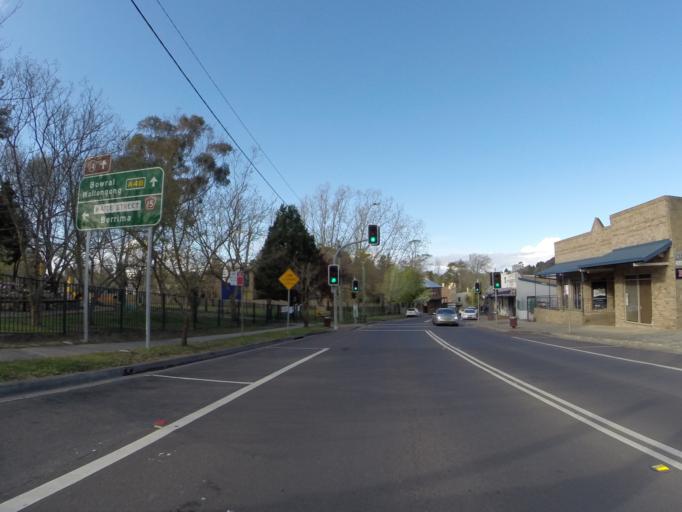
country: AU
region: New South Wales
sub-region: Wingecarribee
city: Moss Vale
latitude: -34.5518
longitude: 150.3670
